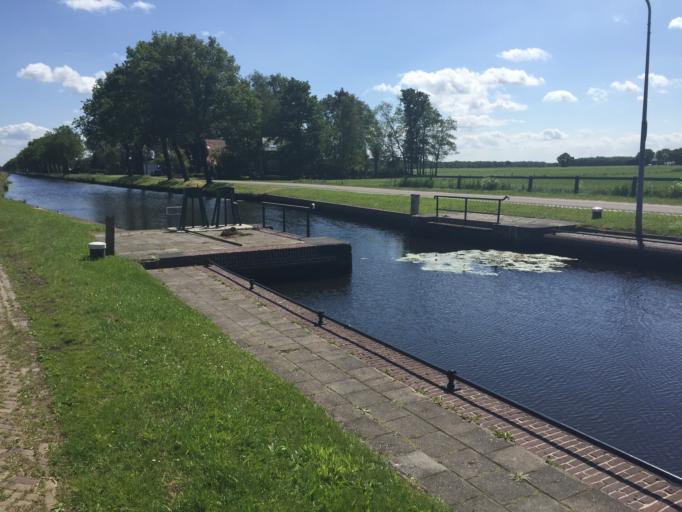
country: NL
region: Friesland
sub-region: Gemeente Heerenveen
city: Jubbega
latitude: 53.0269
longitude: 6.1338
